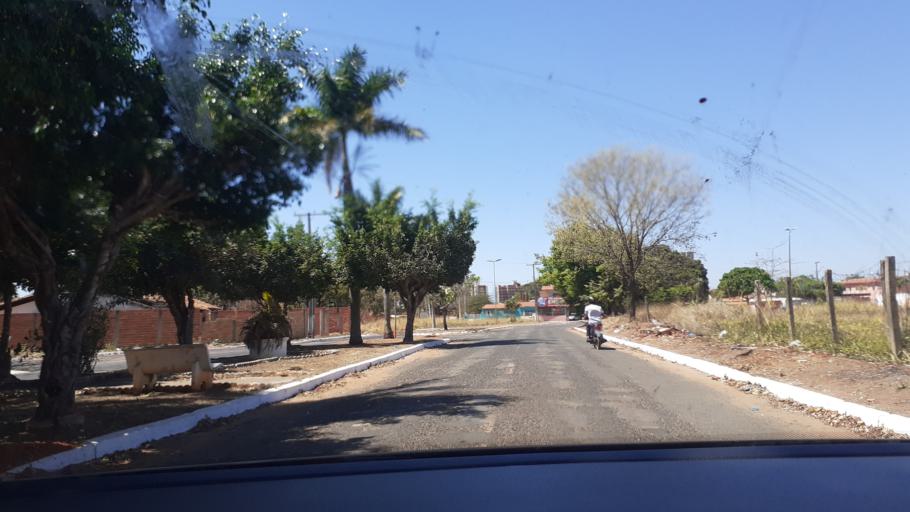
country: BR
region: Goias
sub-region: Caldas Novas
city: Caldas Novas
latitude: -17.7397
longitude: -48.6417
